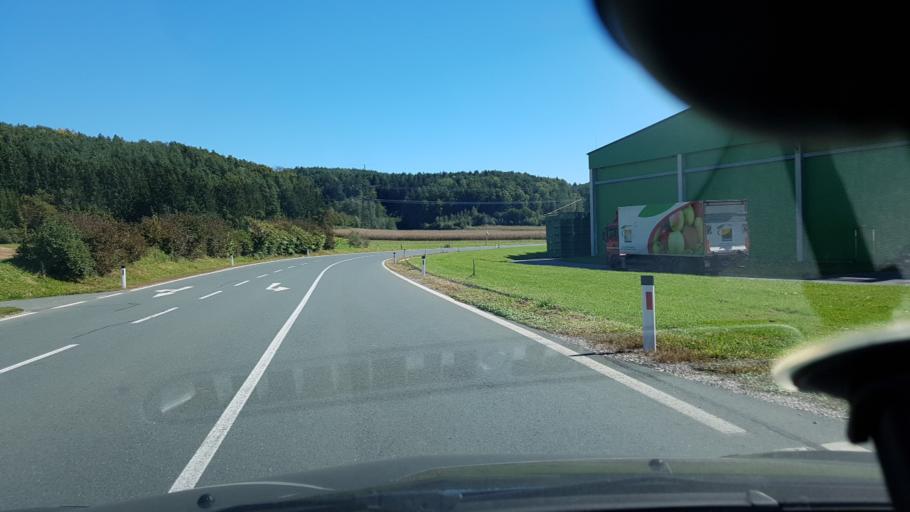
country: AT
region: Styria
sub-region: Politischer Bezirk Weiz
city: Oberrettenbach
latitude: 47.1435
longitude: 15.7836
